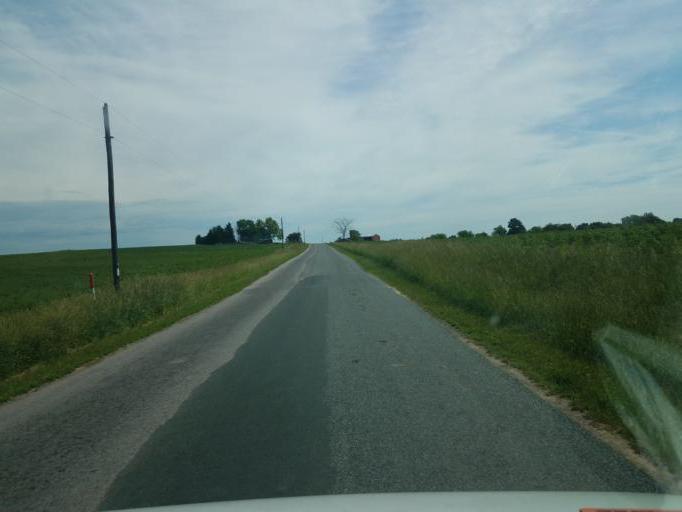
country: US
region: Wisconsin
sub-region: Vernon County
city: Hillsboro
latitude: 43.5604
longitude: -90.3794
